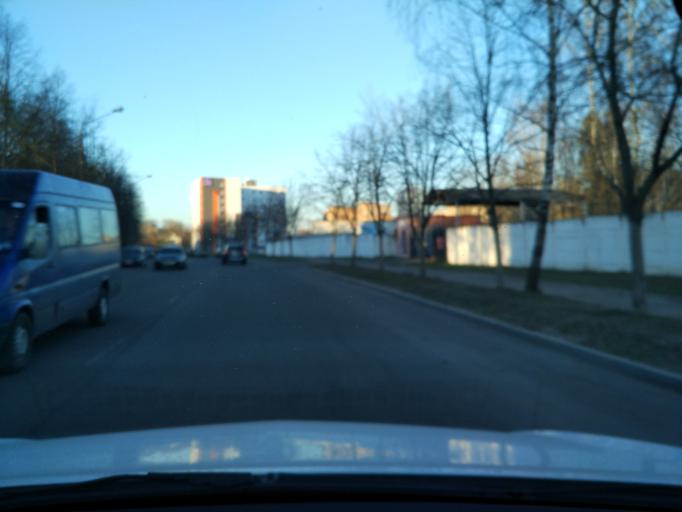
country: BY
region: Minsk
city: Syenitsa
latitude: 53.8655
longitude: 27.5062
